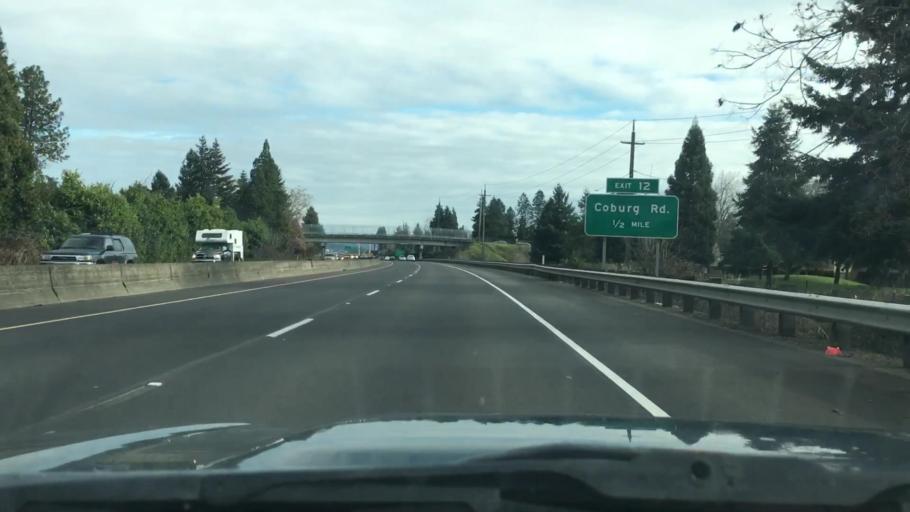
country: US
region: Oregon
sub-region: Lane County
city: Eugene
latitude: 44.0883
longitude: -123.0844
